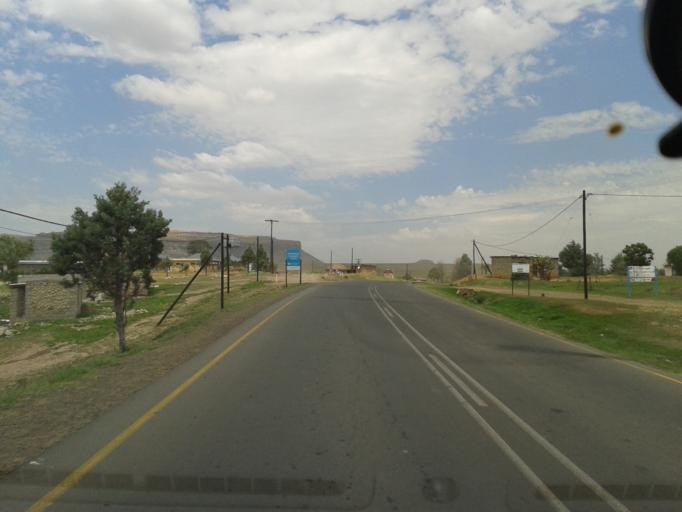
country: LS
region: Maseru
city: Maseru
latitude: -29.3589
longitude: 27.6518
